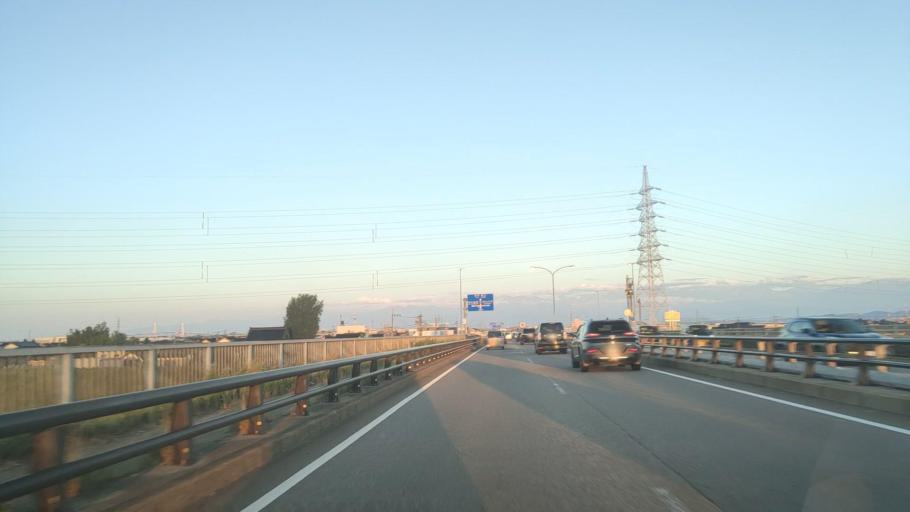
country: JP
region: Toyama
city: Nishishinminato
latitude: 36.7592
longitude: 137.0542
